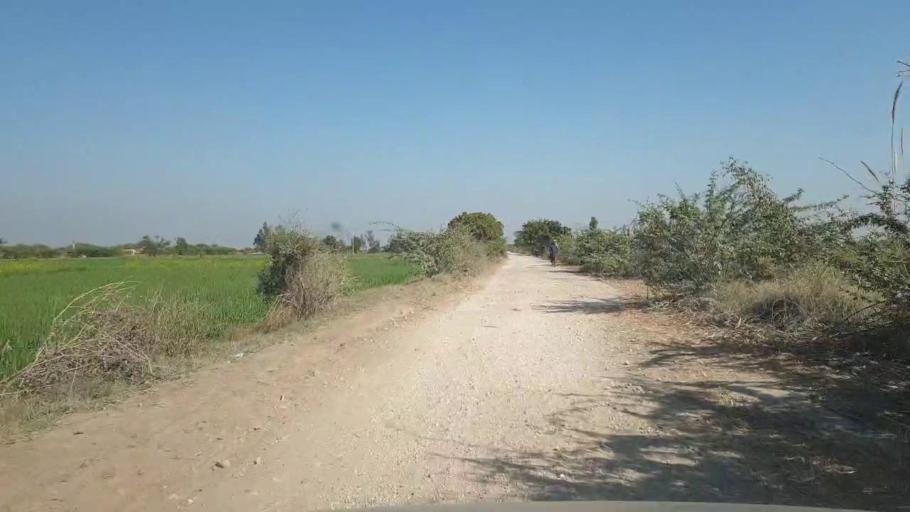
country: PK
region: Sindh
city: Pithoro
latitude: 25.3989
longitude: 69.2622
